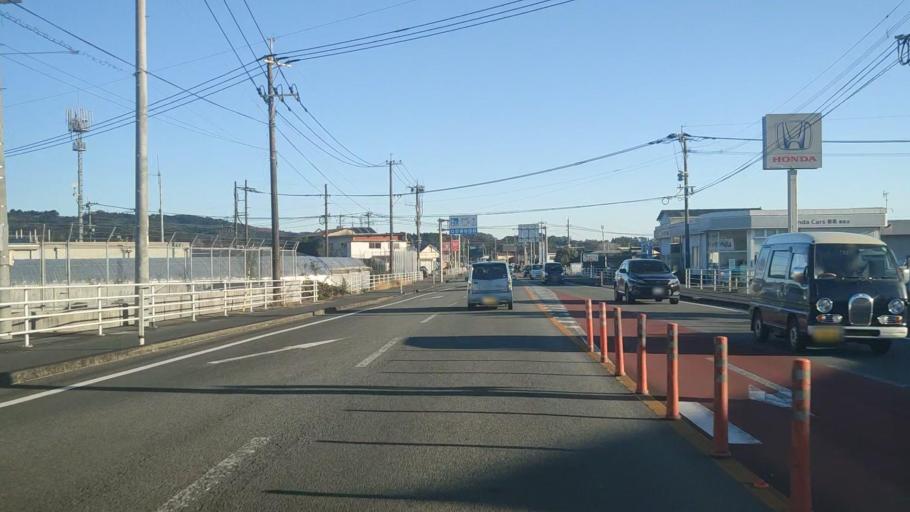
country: JP
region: Miyazaki
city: Takanabe
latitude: 32.2552
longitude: 131.5543
